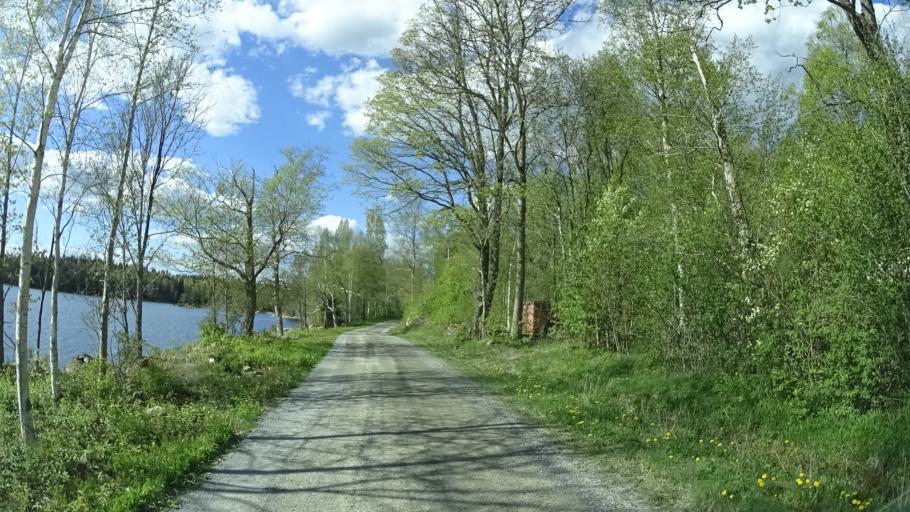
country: SE
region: OErebro
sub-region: Nora Kommun
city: As
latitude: 59.4470
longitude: 14.8104
